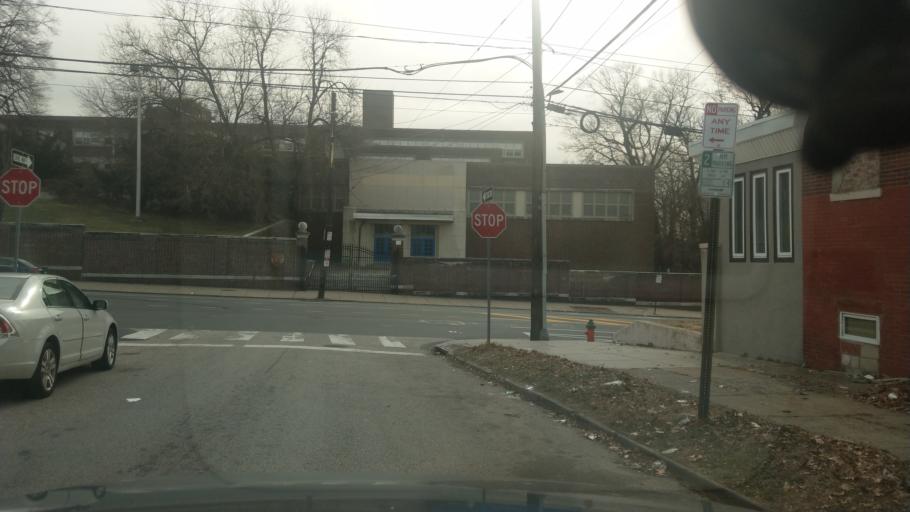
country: US
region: Pennsylvania
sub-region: Montgomery County
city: Wyncote
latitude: 40.0413
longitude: -75.1464
